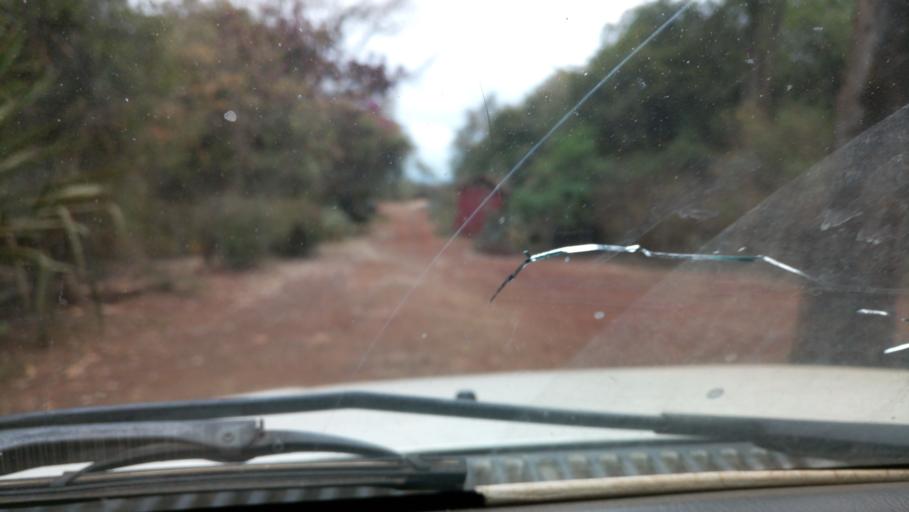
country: KE
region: Kajiado
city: Ngong
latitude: -1.3783
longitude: 36.7545
